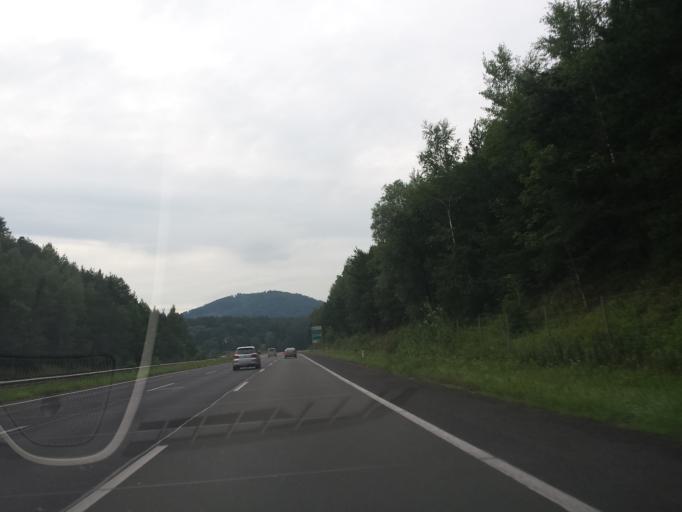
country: AT
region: Styria
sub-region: Politischer Bezirk Graz-Umgebung
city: Gratkorn
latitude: 47.1337
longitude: 15.3573
